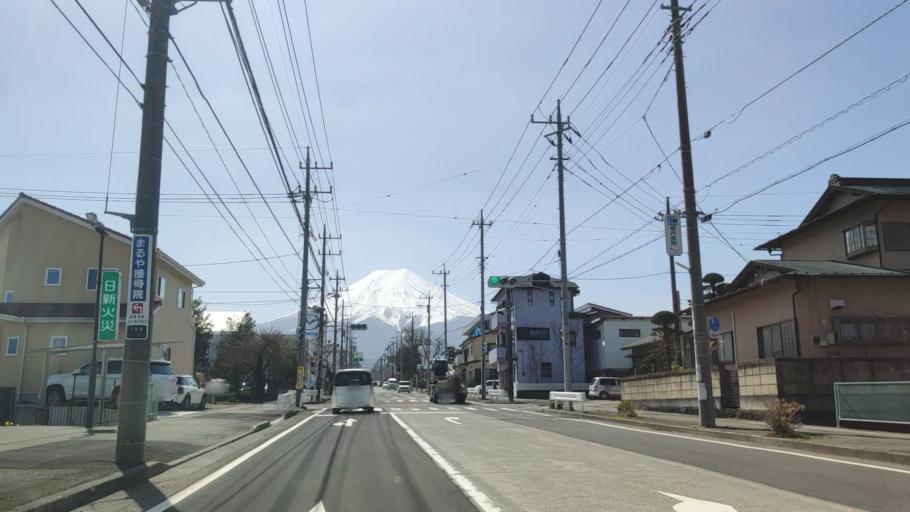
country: JP
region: Yamanashi
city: Fujikawaguchiko
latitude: 35.4903
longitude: 138.8085
